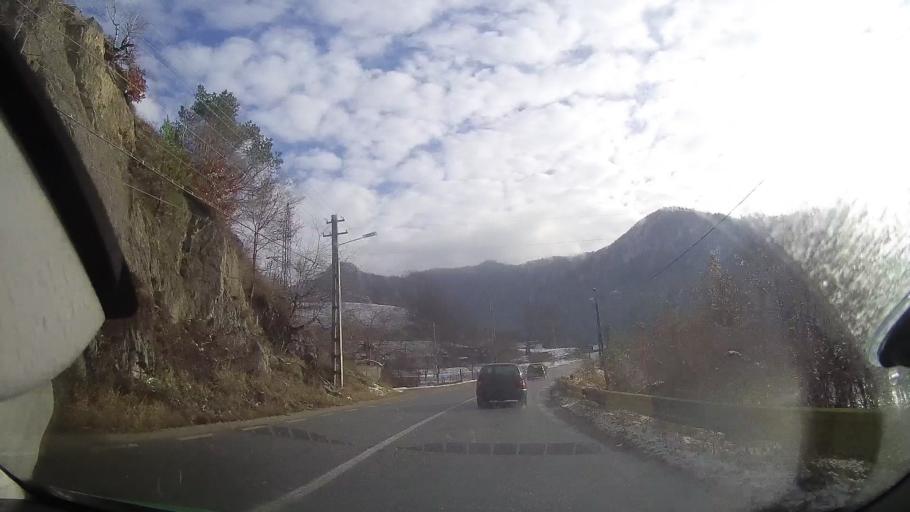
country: RO
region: Alba
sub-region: Oras Baia de Aries
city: Baia de Aries
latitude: 46.3914
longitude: 23.2895
